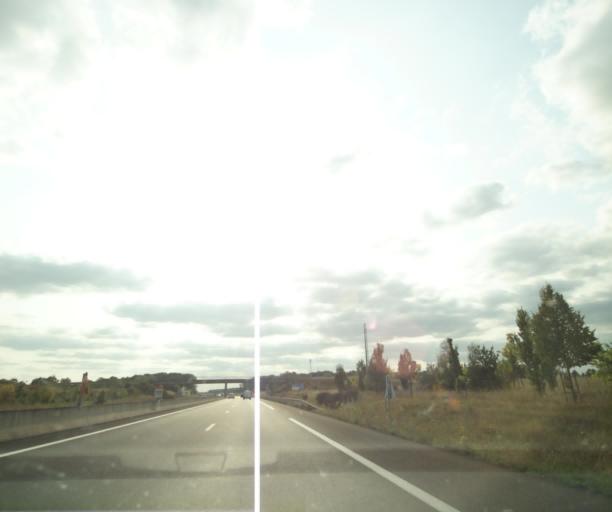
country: FR
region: Centre
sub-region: Departement d'Indre-et-Loire
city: Veigne
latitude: 47.3101
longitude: 0.7237
